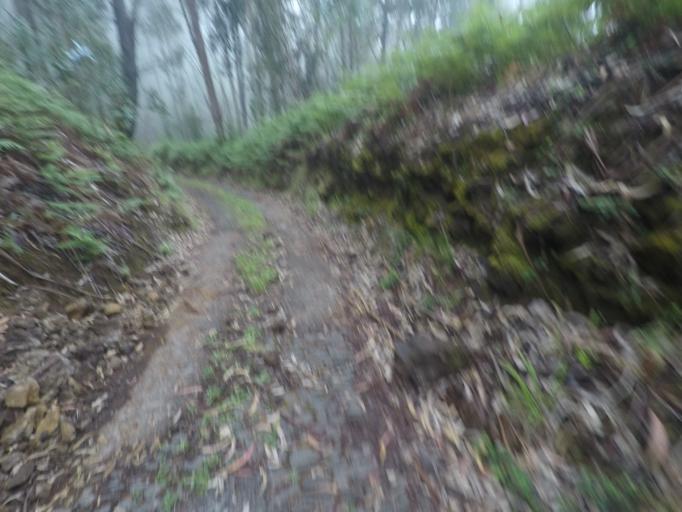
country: PT
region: Madeira
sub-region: Calheta
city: Arco da Calheta
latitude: 32.7268
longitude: -17.0958
